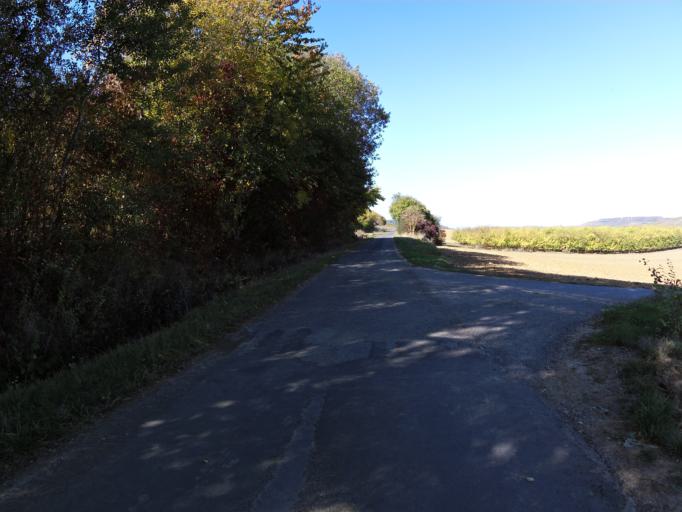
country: DE
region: Bavaria
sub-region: Regierungsbezirk Unterfranken
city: Eibelstadt
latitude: 49.7135
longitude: 9.9972
